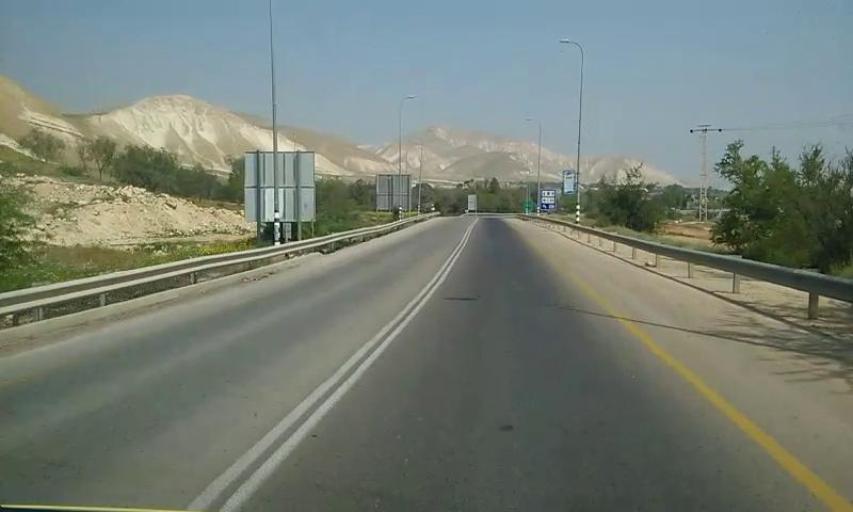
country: PS
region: West Bank
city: Al Fasayil
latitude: 32.0510
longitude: 35.4648
